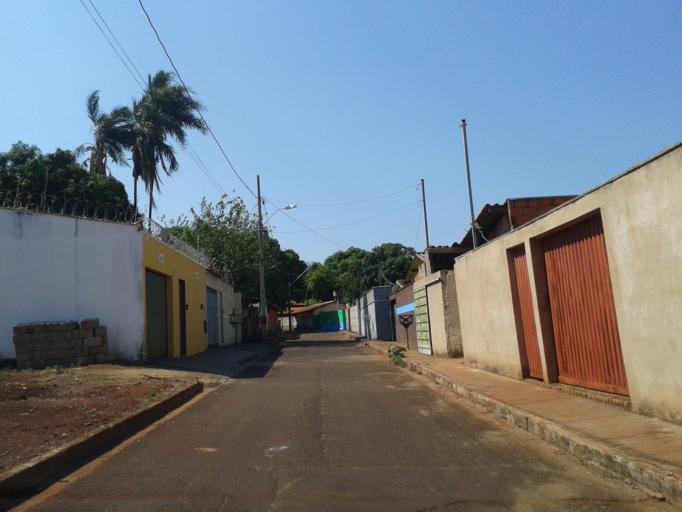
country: BR
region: Minas Gerais
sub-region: Ituiutaba
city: Ituiutaba
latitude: -18.9571
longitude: -49.4533
